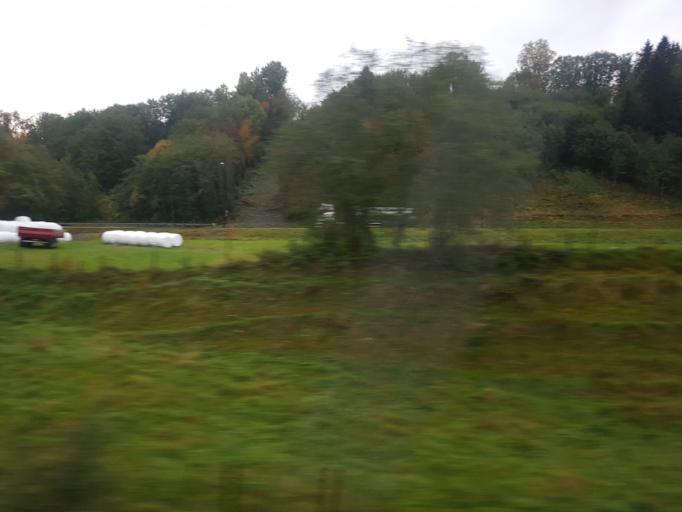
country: NO
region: Sor-Trondelag
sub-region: Melhus
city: Lundamo
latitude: 63.1383
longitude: 10.2605
